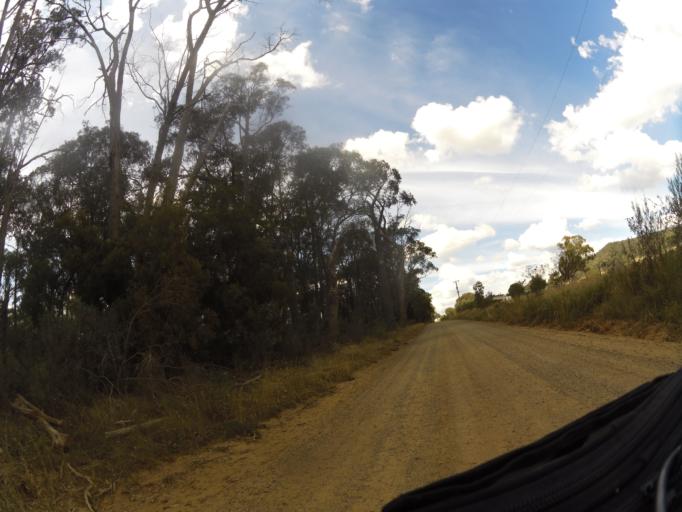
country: AU
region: Victoria
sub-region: Benalla
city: Benalla
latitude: -36.7792
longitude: 145.9770
